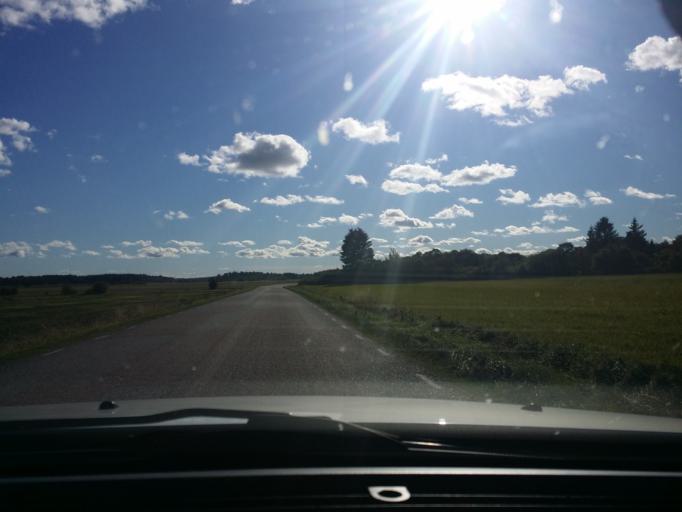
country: SE
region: Vaestmanland
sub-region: Vasteras
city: Vasteras
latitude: 59.5566
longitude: 16.4704
